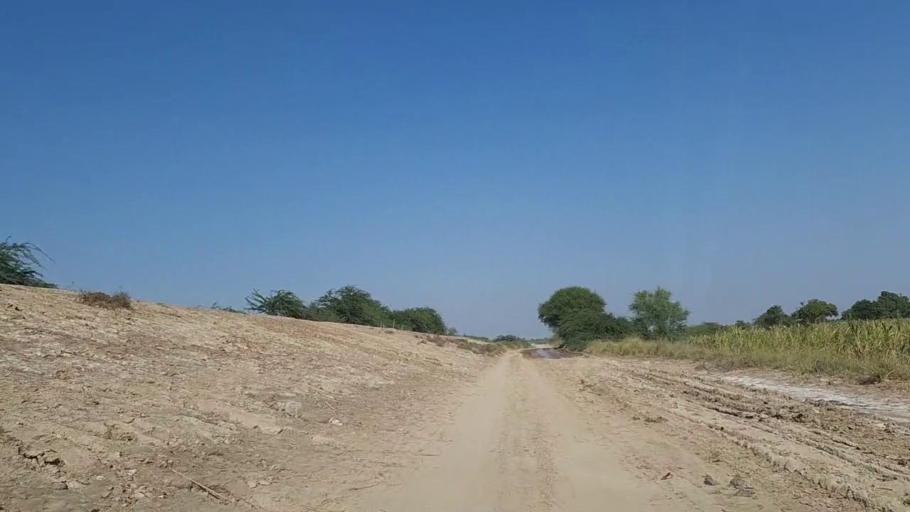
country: PK
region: Sindh
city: Thatta
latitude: 24.5862
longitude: 68.0383
